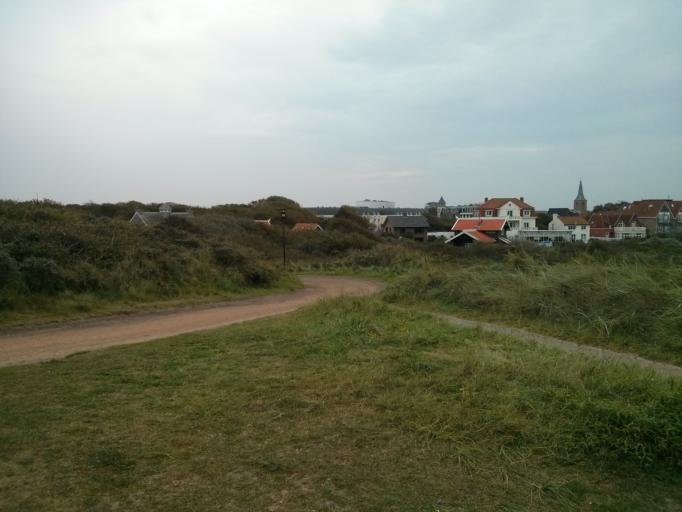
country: NL
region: Zeeland
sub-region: Gemeente Middelburg
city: Middelburg
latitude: 51.5672
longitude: 3.4997
